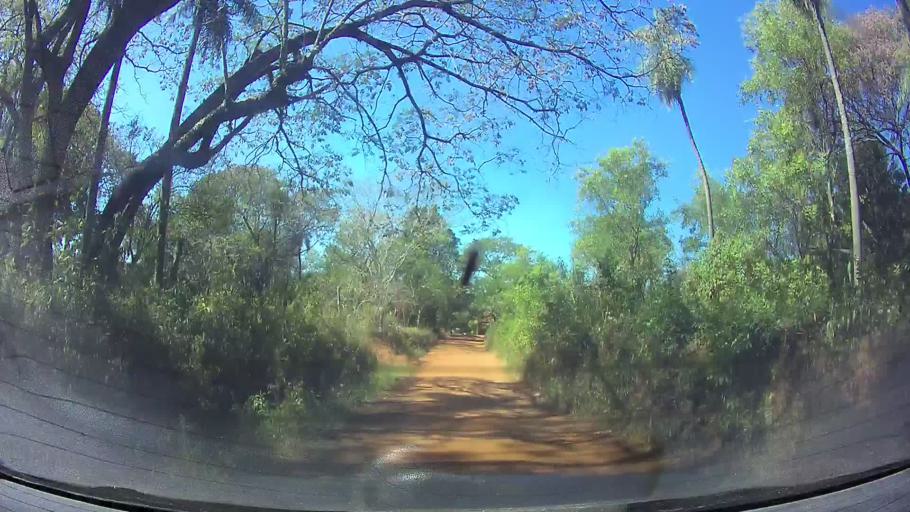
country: PY
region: Central
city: Limpio
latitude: -25.2443
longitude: -57.4483
